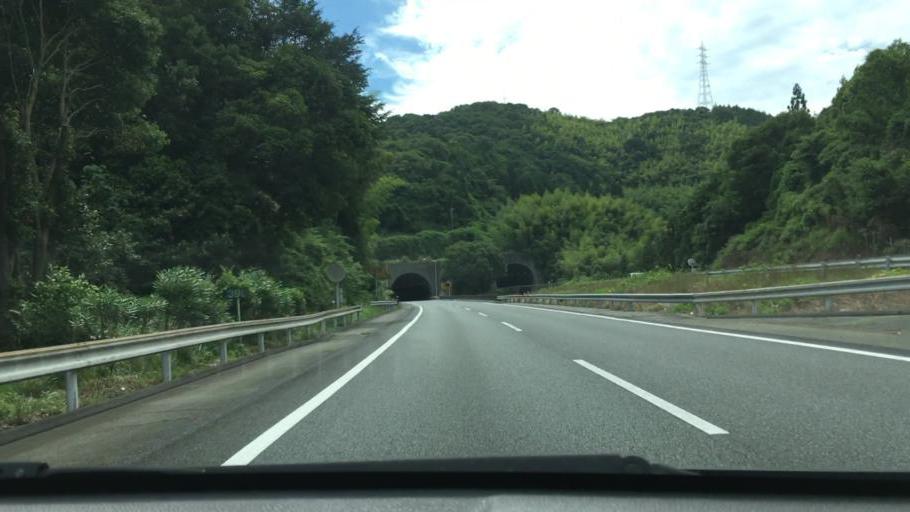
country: JP
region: Yamaguchi
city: Hofu
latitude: 34.0725
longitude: 131.6744
